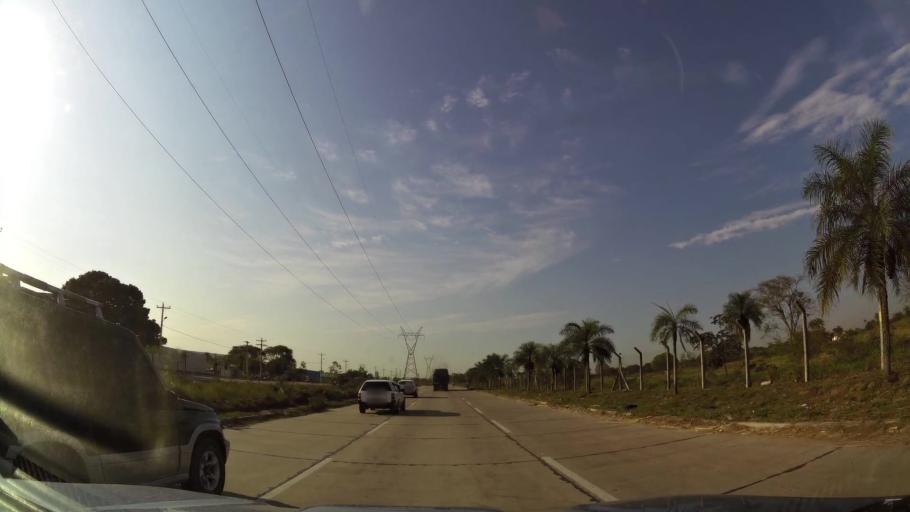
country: BO
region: Santa Cruz
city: Santa Cruz de la Sierra
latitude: -17.6996
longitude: -63.1336
